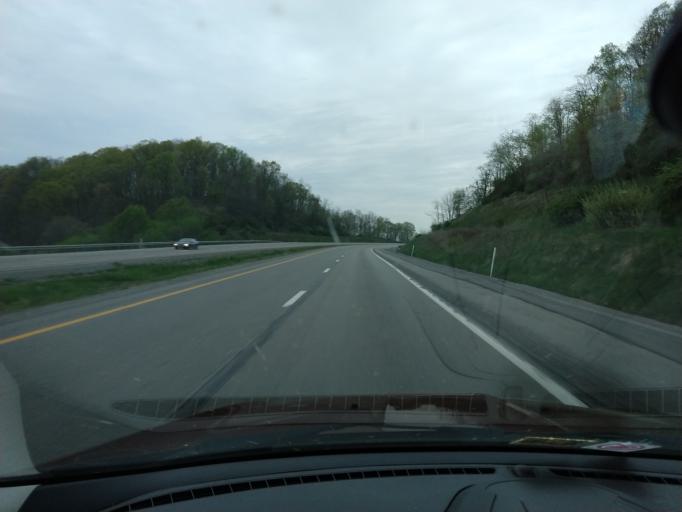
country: US
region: West Virginia
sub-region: Lewis County
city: Weston
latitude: 38.9323
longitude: -80.5436
